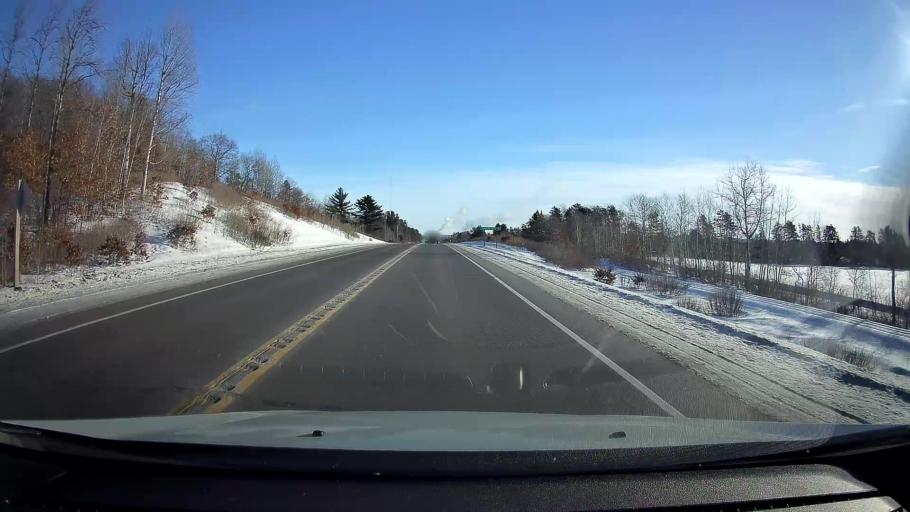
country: US
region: Wisconsin
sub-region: Sawyer County
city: Hayward
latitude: 45.9821
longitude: -91.5544
